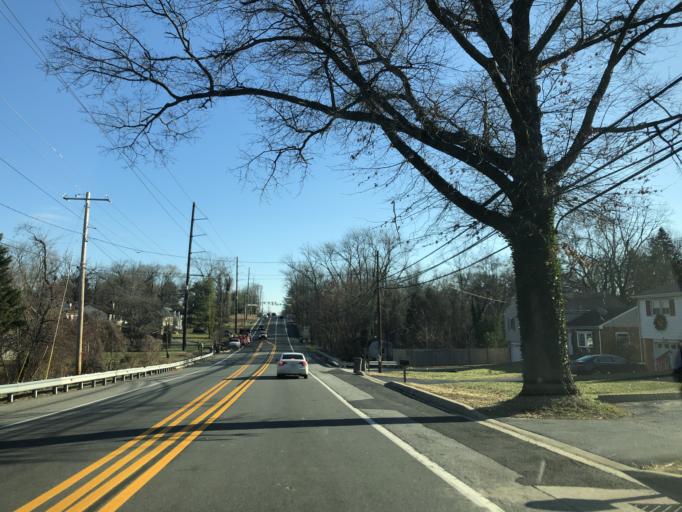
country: US
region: Delaware
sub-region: New Castle County
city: Elsmere
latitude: 39.7479
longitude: -75.6470
